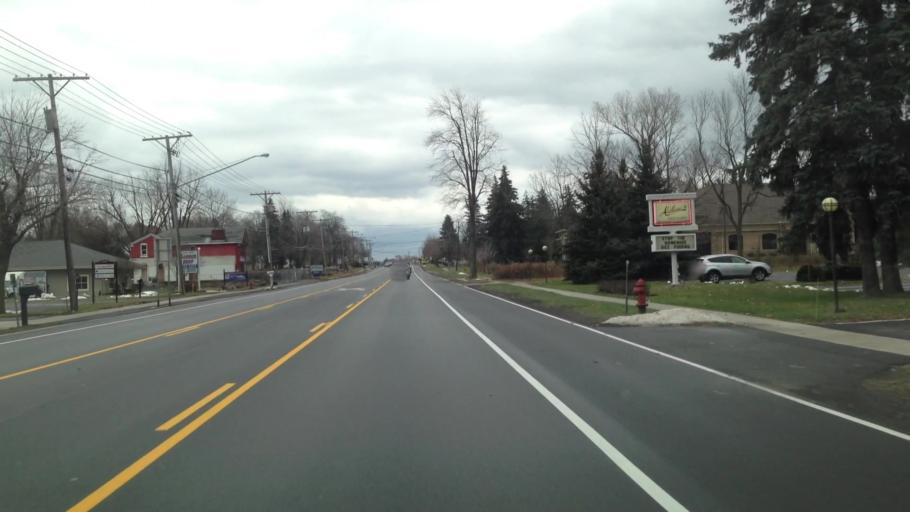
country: US
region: New York
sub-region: Erie County
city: Harris Hill
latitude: 42.9650
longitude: -78.6857
